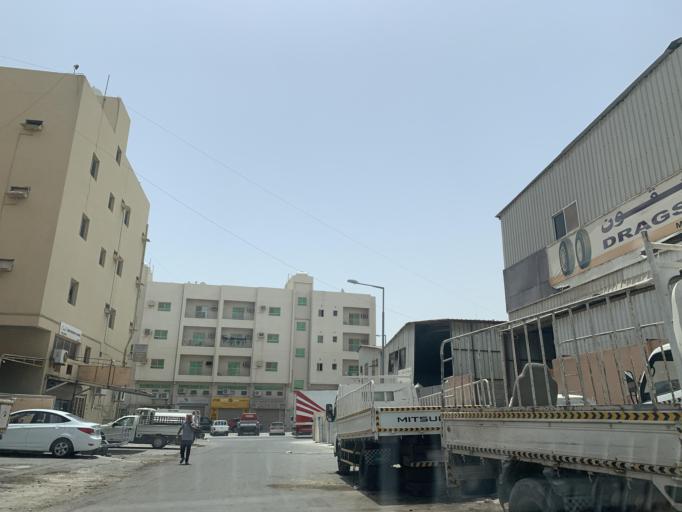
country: BH
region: Northern
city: Ar Rifa'
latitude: 26.1371
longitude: 50.5863
